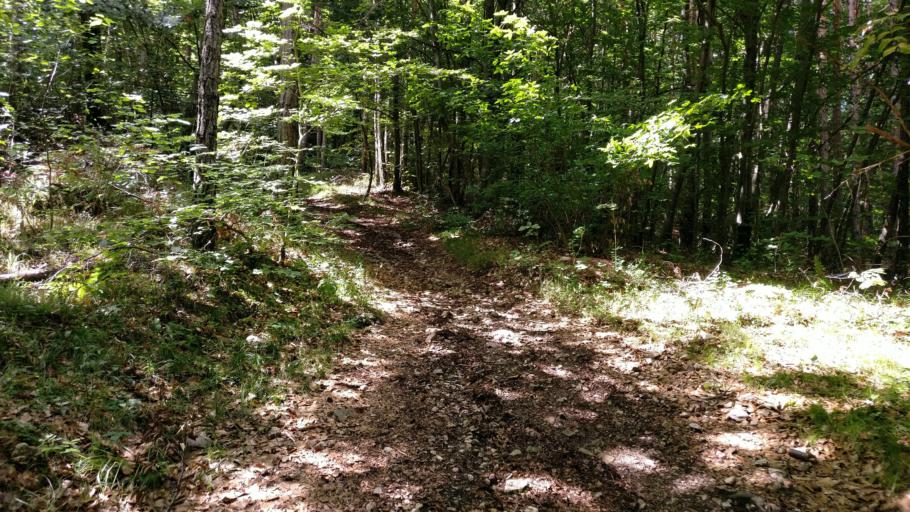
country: IT
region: Trentino-Alto Adige
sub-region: Bolzano
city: San Paolo
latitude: 46.4732
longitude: 11.2367
